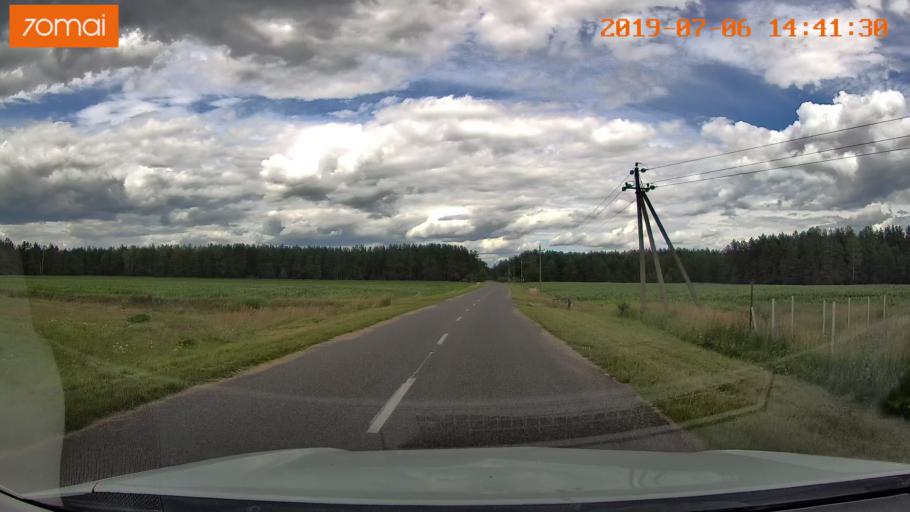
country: BY
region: Minsk
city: Ivyanyets
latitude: 53.9329
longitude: 26.6784
